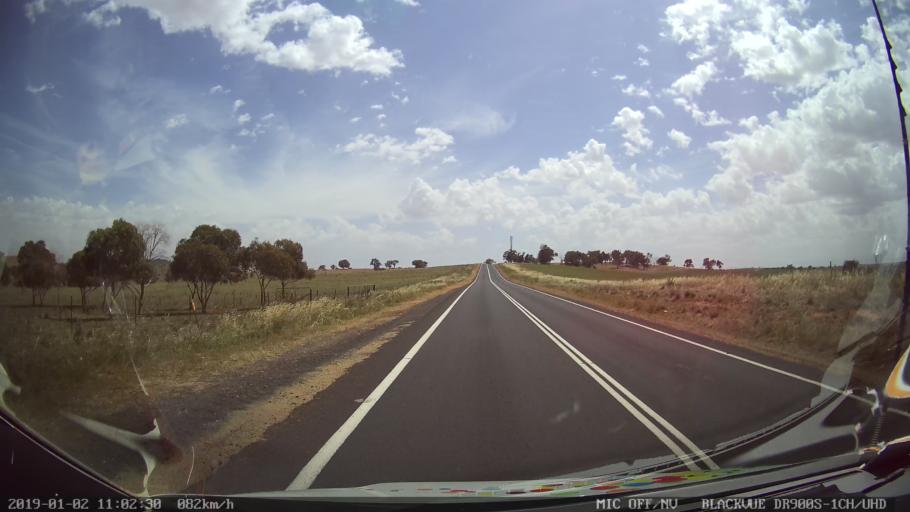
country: AU
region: New South Wales
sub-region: Young
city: Young
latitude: -34.5851
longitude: 148.3272
